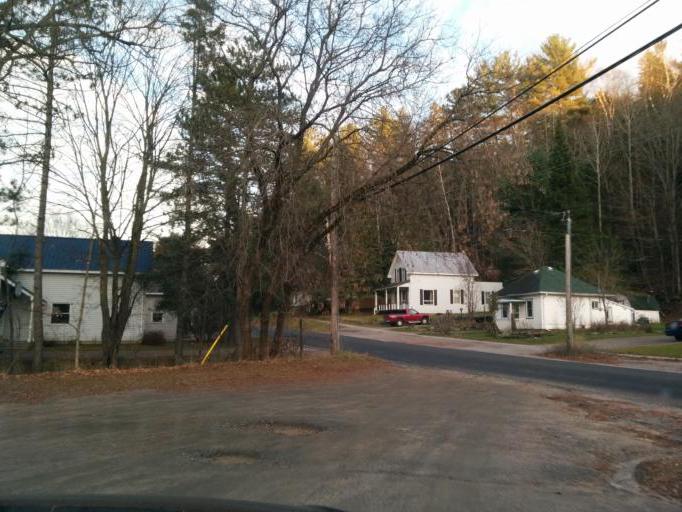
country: CA
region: Ontario
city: Bancroft
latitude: 45.0441
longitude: -78.5130
